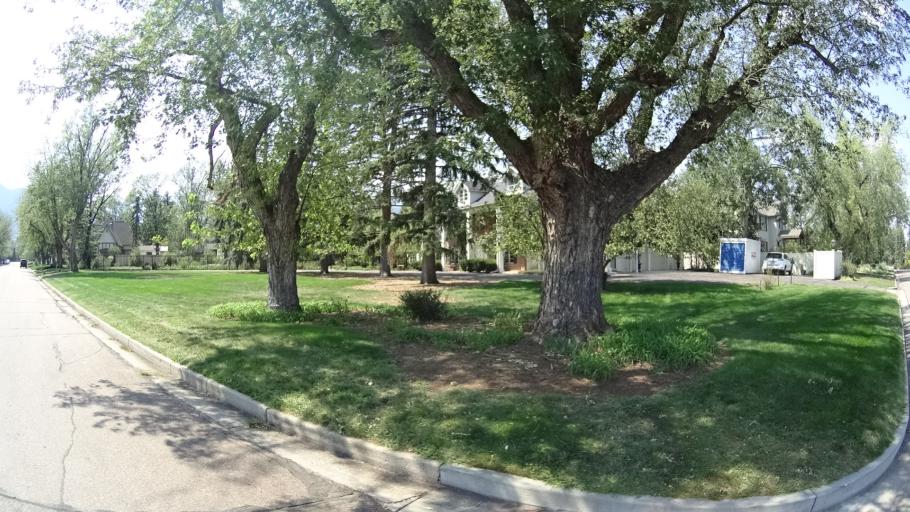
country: US
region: Colorado
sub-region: El Paso County
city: Colorado Springs
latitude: 38.7955
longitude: -104.8448
